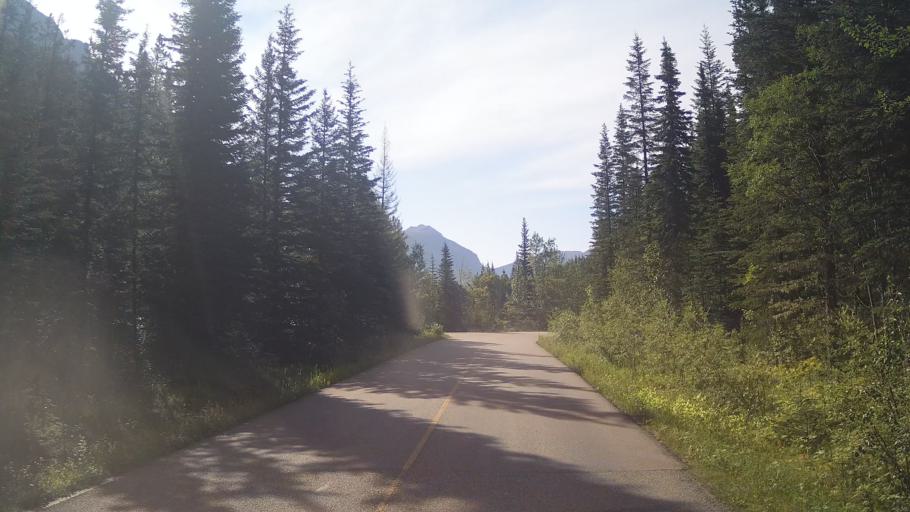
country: CA
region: Alberta
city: Hinton
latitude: 53.1746
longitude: -117.8289
